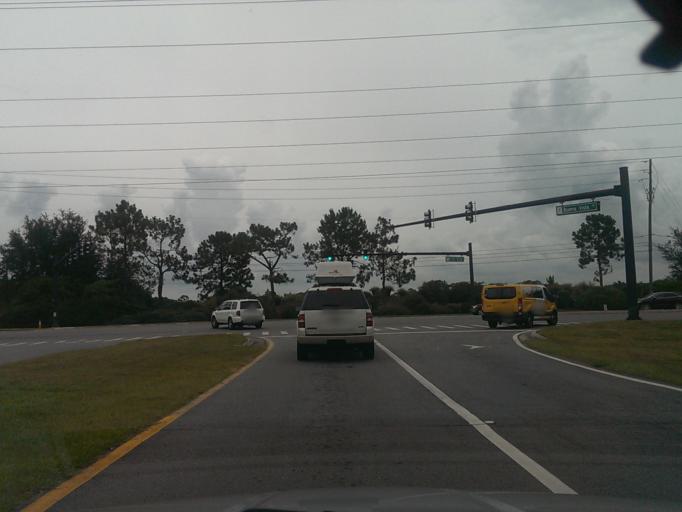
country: US
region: Florida
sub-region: Orange County
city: Doctor Phillips
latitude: 28.3981
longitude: -81.5258
